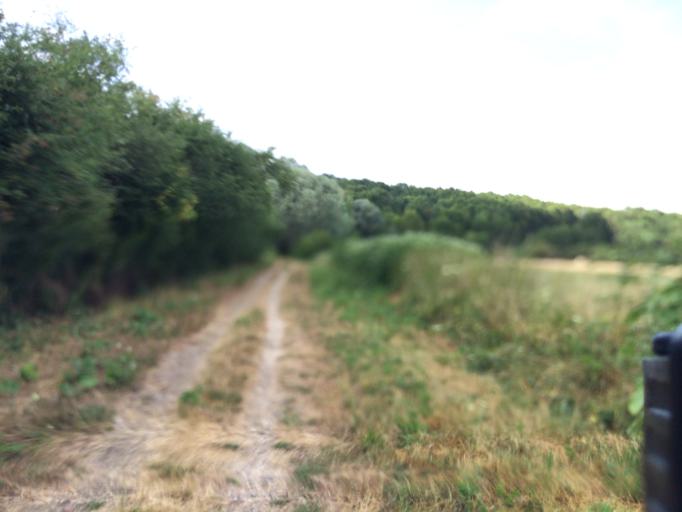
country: FR
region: Ile-de-France
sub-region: Departement de l'Essonne
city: Etiolles
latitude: 48.6387
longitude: 2.4919
